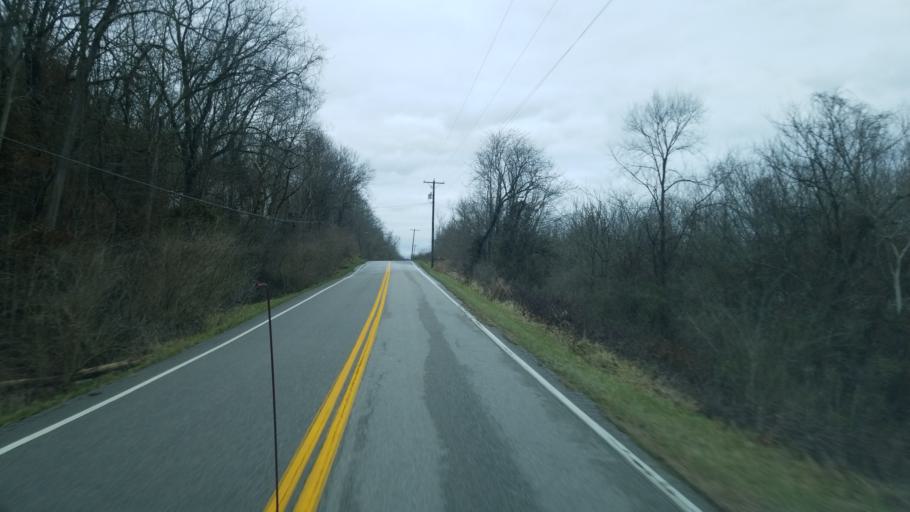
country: US
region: Ohio
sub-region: Clermont County
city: New Richmond
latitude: 38.9214
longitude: -84.2694
